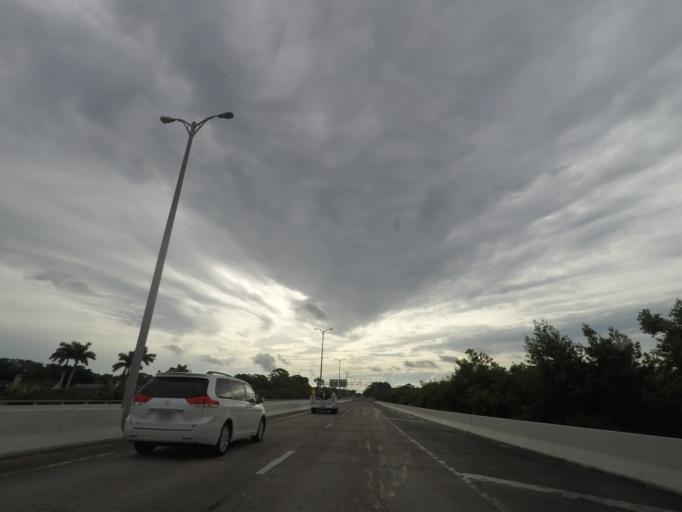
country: US
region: Florida
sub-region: Pinellas County
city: Redington Shores
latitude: 27.8438
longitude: -82.8363
